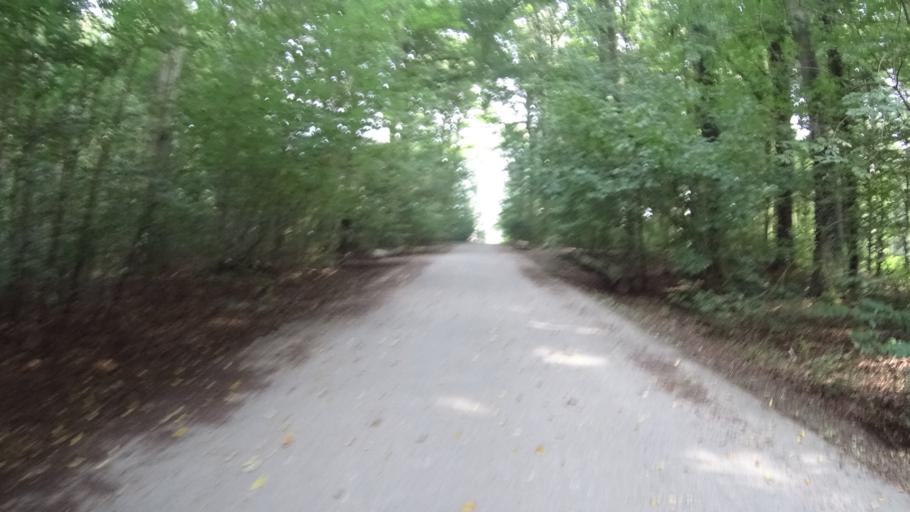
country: DE
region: North Rhine-Westphalia
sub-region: Regierungsbezirk Arnsberg
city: Dortmund
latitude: 51.4855
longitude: 7.4550
